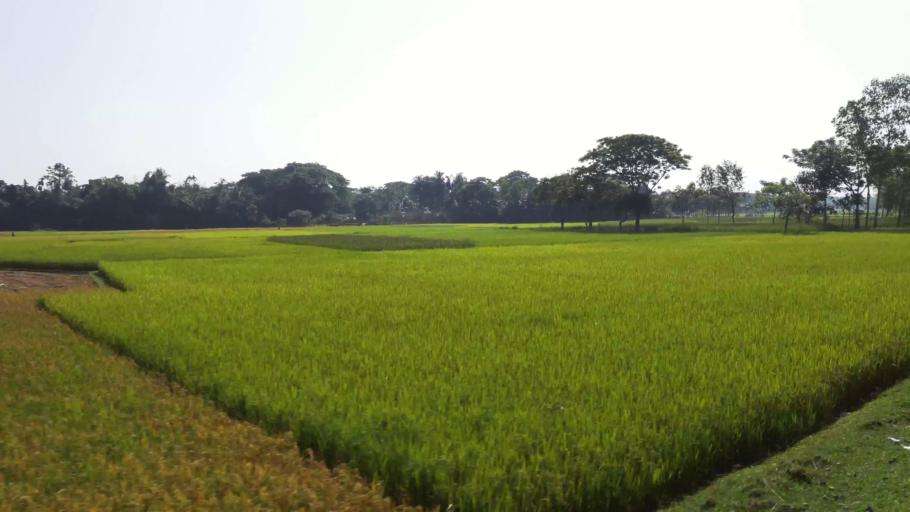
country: BD
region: Dhaka
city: Gafargaon
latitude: 24.5766
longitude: 90.5080
